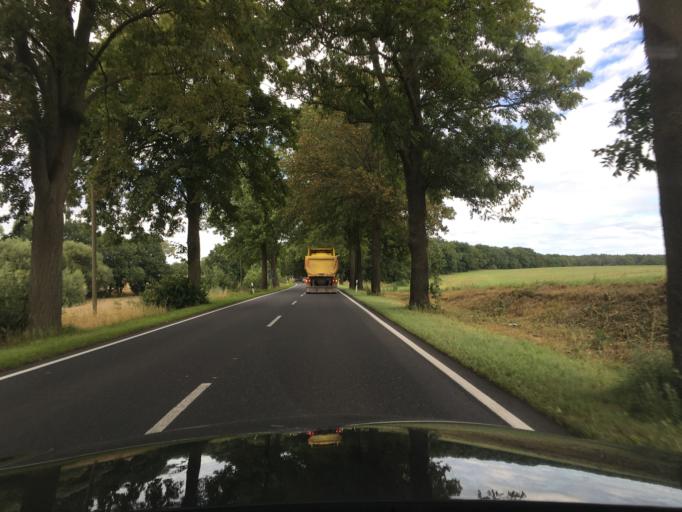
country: DE
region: Brandenburg
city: Gransee
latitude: 52.9085
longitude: 13.1583
